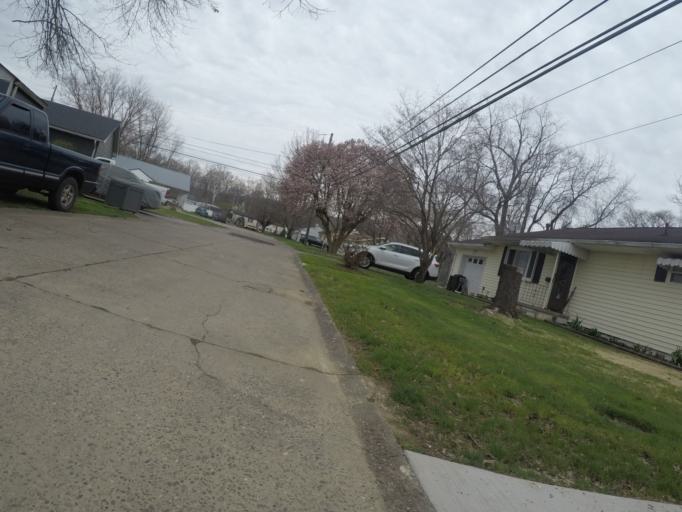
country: US
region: West Virginia
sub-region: Cabell County
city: Barboursville
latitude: 38.4168
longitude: -82.2971
